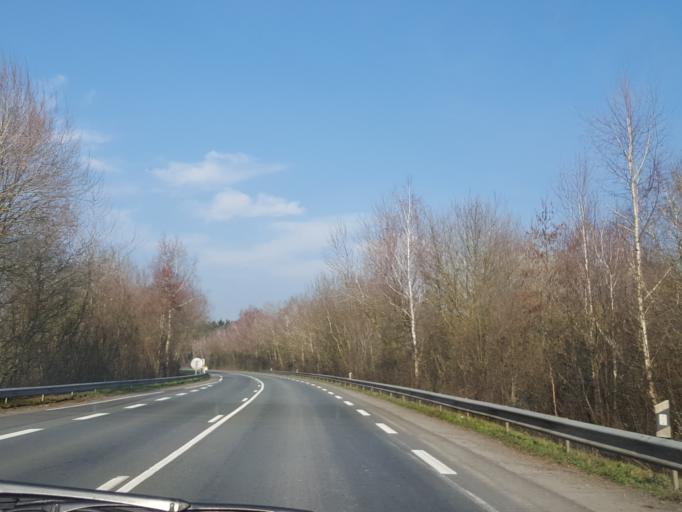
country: FR
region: Pays de la Loire
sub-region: Departement de la Vendee
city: Saint-Fulgent
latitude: 46.8493
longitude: -1.1632
